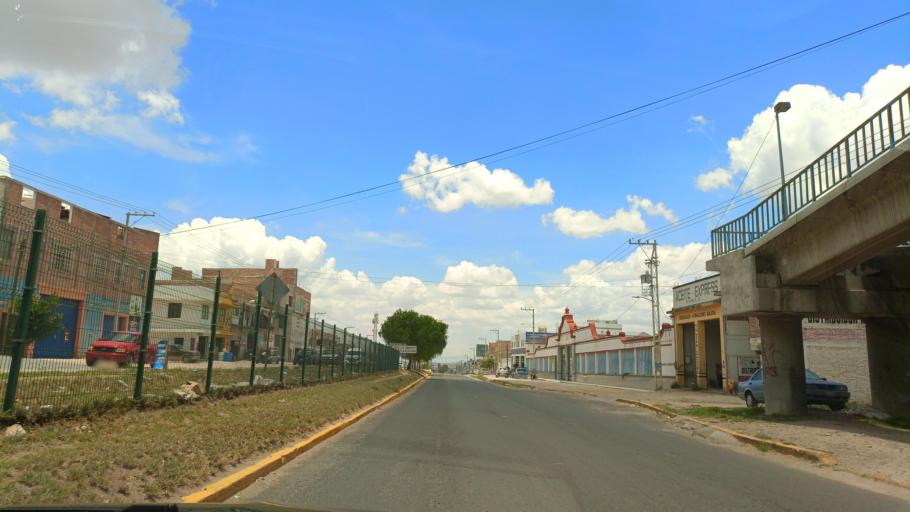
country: MX
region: Guerrero
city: San Luis de la Paz
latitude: 21.2887
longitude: -100.5103
